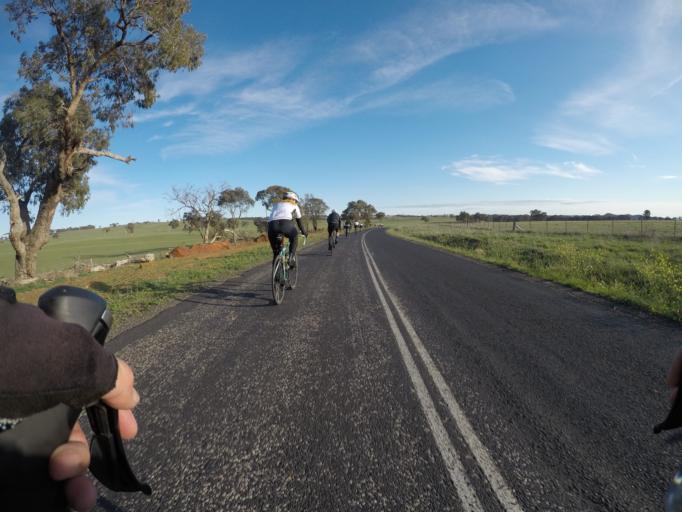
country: AU
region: New South Wales
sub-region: Cabonne
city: Molong
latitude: -33.0021
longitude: 148.7857
